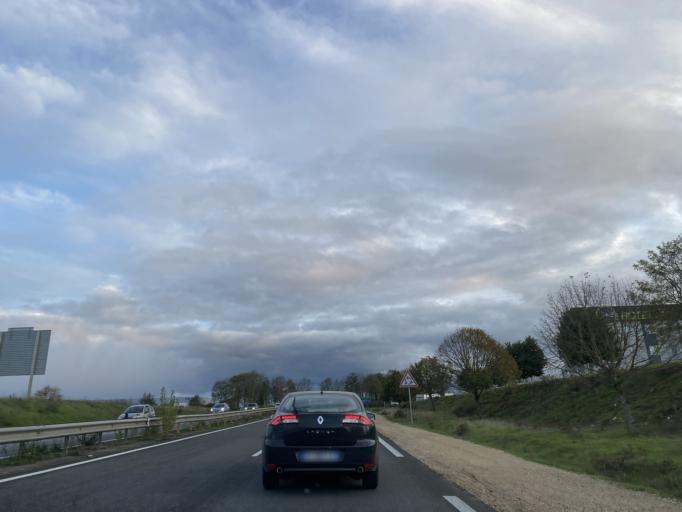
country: FR
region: Centre
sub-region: Departement du Cher
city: La Chapelle-Saint-Ursin
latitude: 47.0481
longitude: 2.3422
